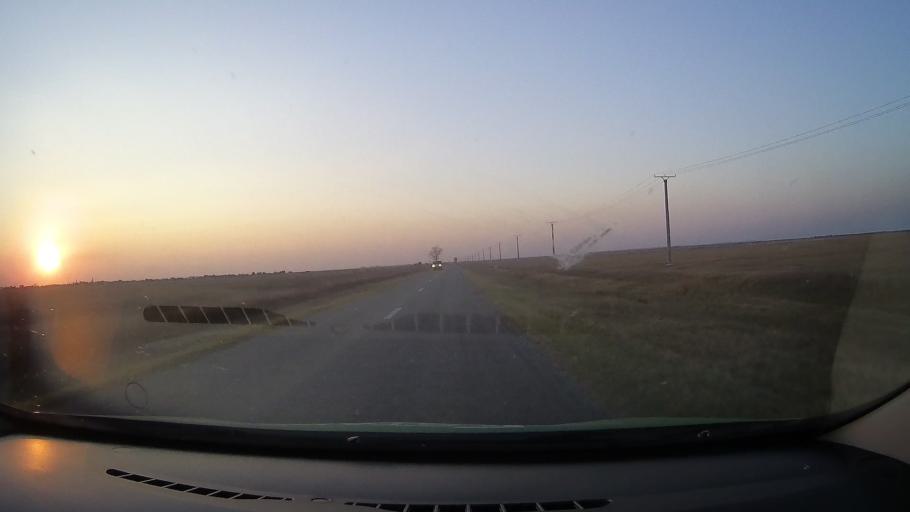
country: RO
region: Arad
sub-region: Comuna Zarand
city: Zarand
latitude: 46.4147
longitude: 21.6252
